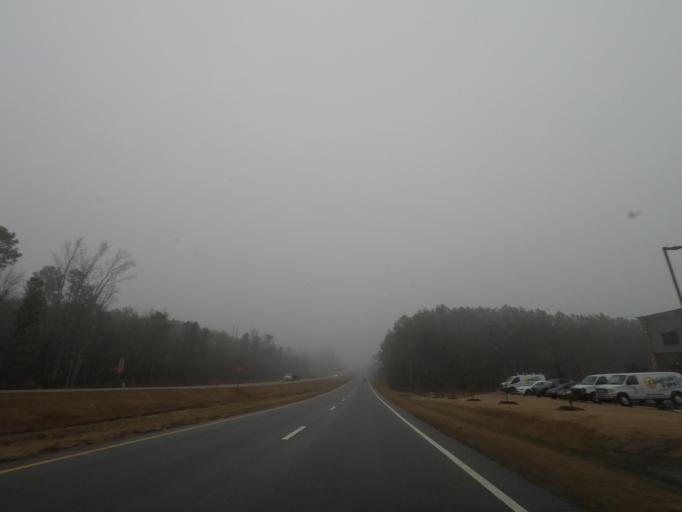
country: US
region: North Carolina
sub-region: Lee County
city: Sanford
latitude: 35.4014
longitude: -79.2316
